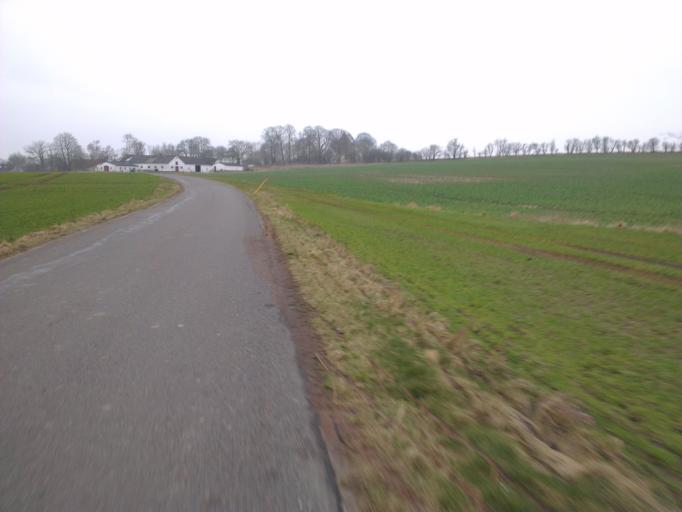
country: DK
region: Capital Region
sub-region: Frederikssund Kommune
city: Frederikssund
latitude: 55.7862
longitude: 12.0231
